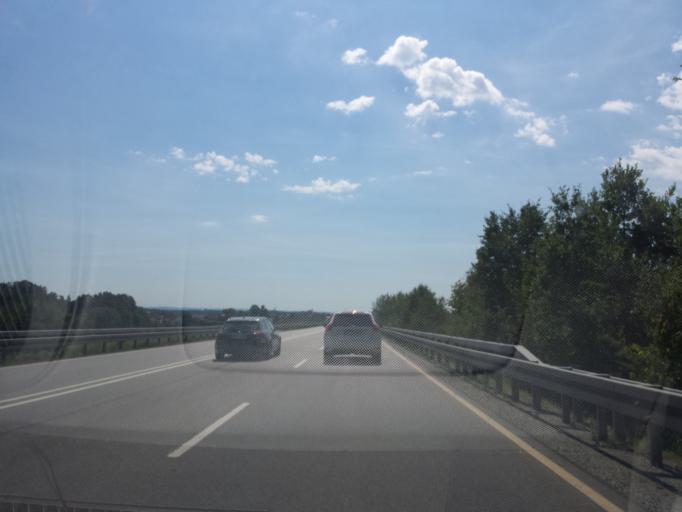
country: DE
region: Bavaria
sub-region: Lower Bavaria
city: Steinach
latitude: 48.9698
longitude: 12.6256
